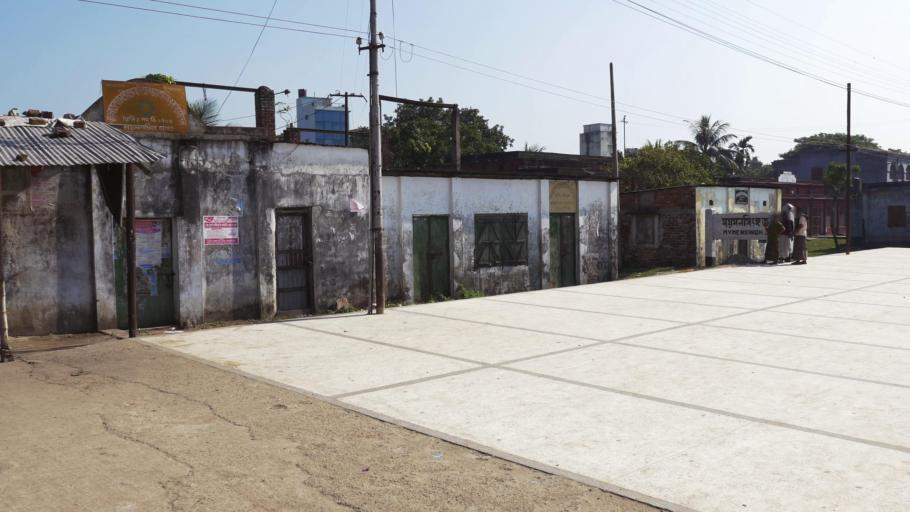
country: BD
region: Dhaka
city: Mymensingh
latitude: 24.6980
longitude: 90.4508
